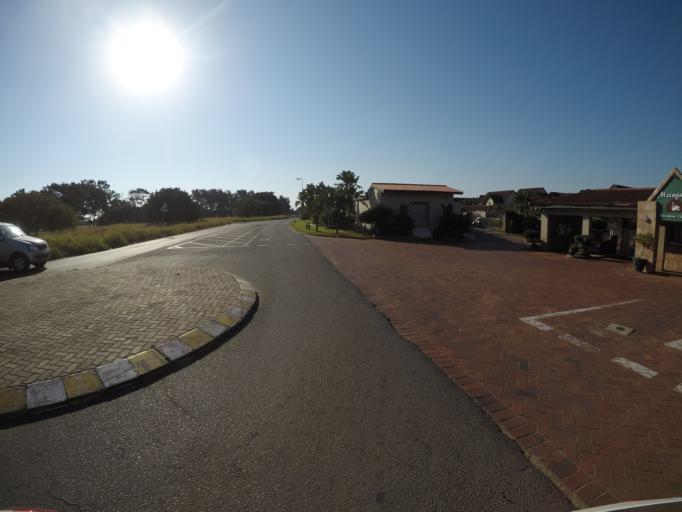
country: ZA
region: KwaZulu-Natal
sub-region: uThungulu District Municipality
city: Richards Bay
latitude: -28.7928
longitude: 32.0811
